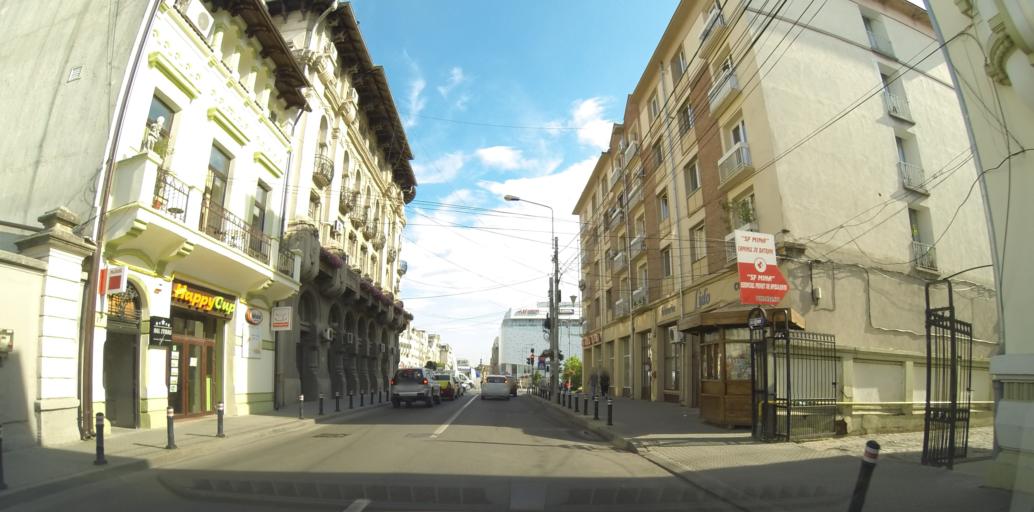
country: RO
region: Dolj
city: Craiova
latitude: 44.3187
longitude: 23.7946
